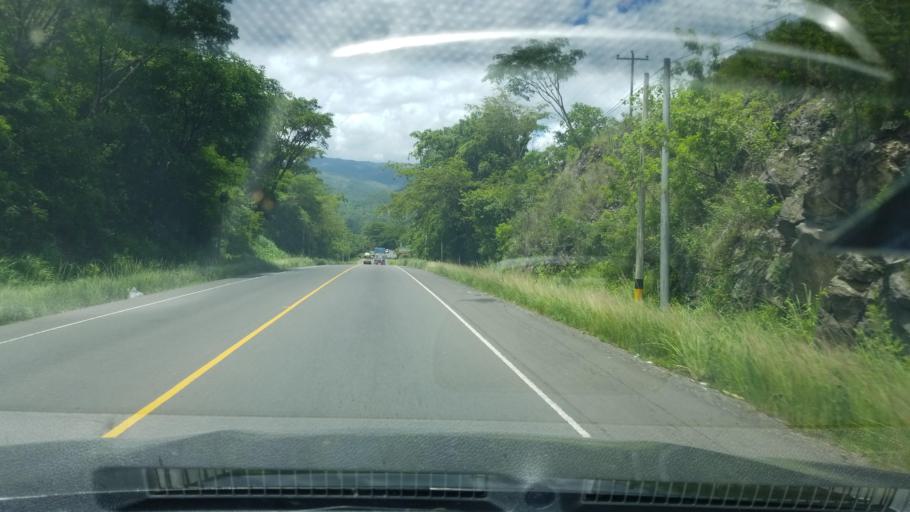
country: HN
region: Francisco Morazan
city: Cofradia
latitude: 14.1996
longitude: -87.2096
